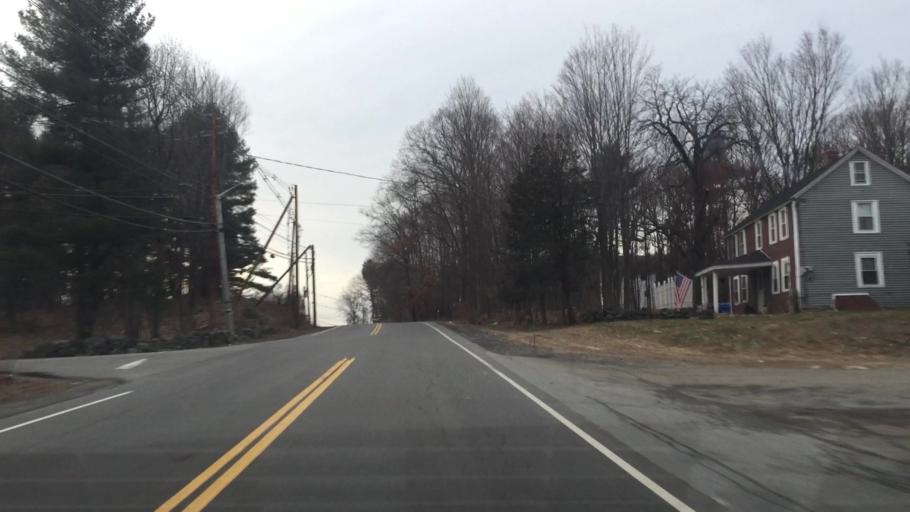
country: US
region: New Hampshire
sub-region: Hillsborough County
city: Pelham
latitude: 42.7469
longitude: -71.2784
